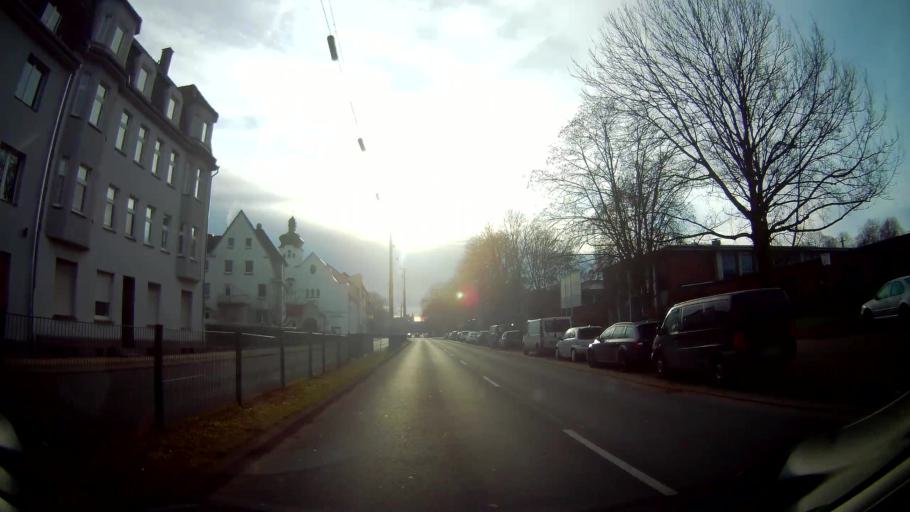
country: DE
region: North Rhine-Westphalia
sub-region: Regierungsbezirk Arnsberg
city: Herne
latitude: 51.5462
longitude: 7.2145
